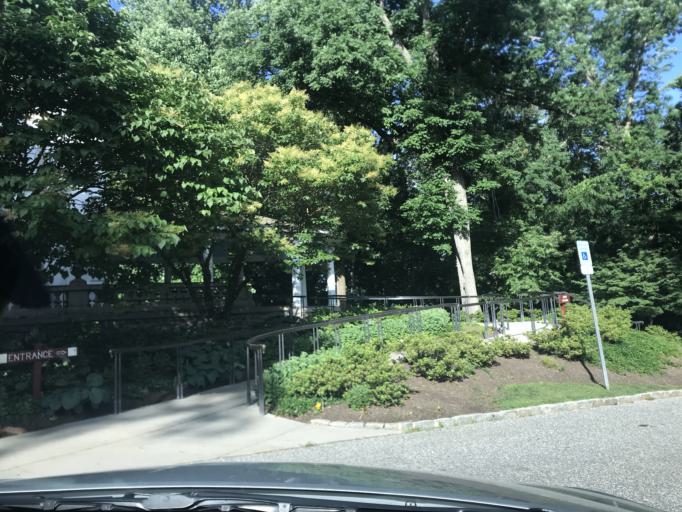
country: US
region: Maryland
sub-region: Harford County
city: North Bel Air
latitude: 39.5345
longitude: -76.3604
